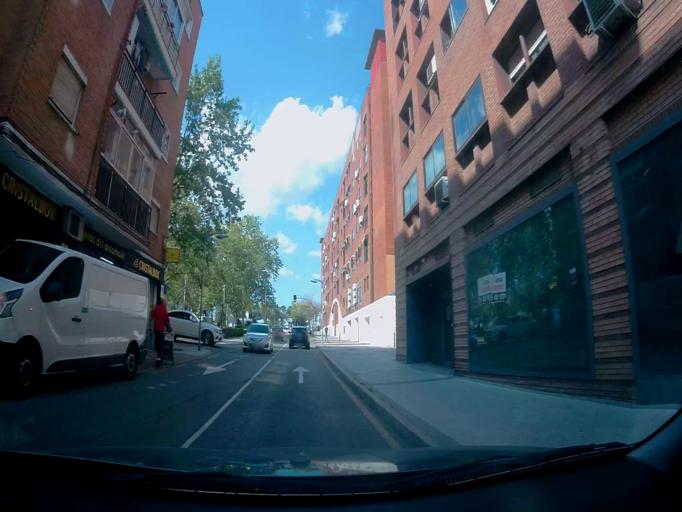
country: ES
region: Madrid
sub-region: Provincia de Madrid
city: Alcorcon
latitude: 40.3507
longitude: -3.8295
